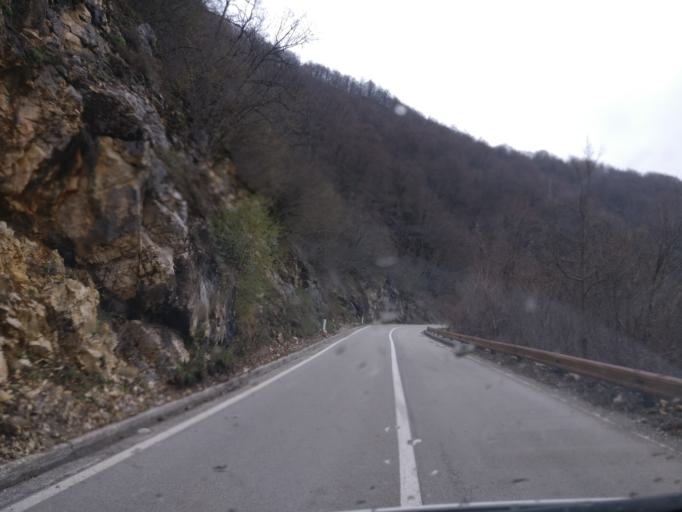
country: ME
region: Opstina Pluzine
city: Pluzine
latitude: 43.1439
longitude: 18.8310
